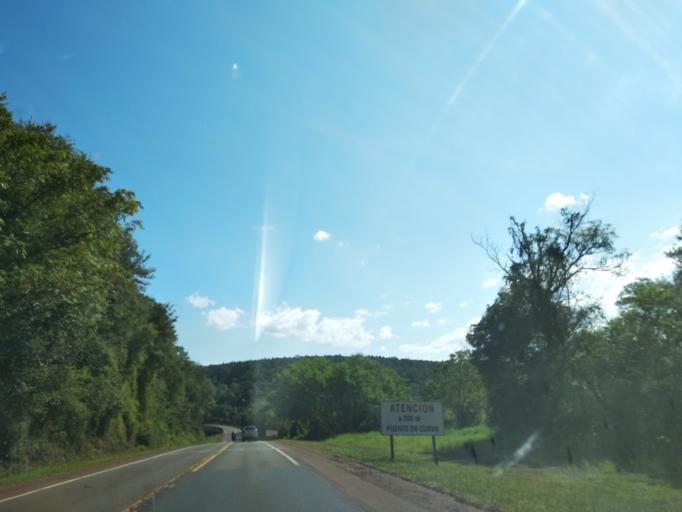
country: AR
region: Misiones
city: Puerto Piray
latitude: -26.4801
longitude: -54.6536
